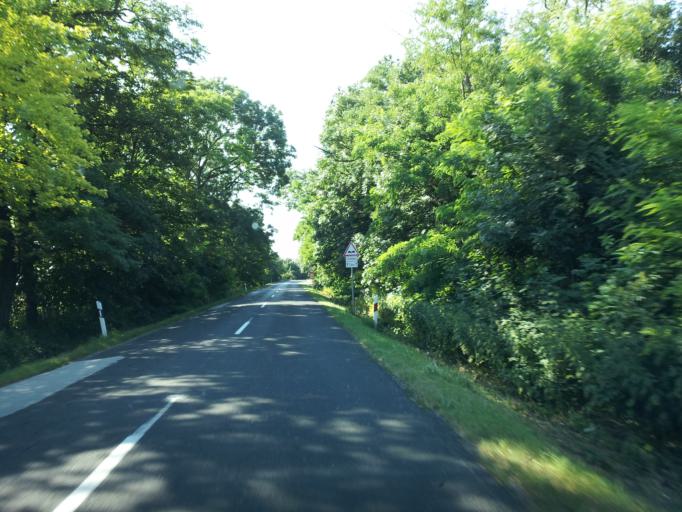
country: HU
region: Fejer
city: Bicske
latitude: 47.4054
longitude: 18.5852
